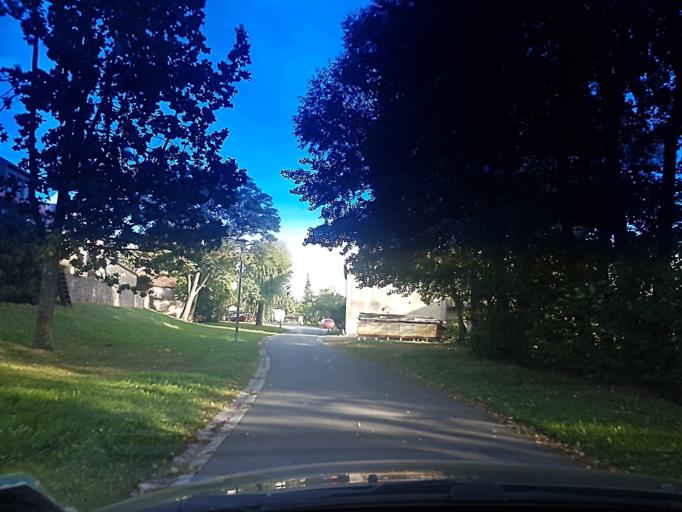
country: DE
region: Bavaria
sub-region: Upper Franconia
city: Schlusselfeld
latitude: 49.7562
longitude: 10.6171
